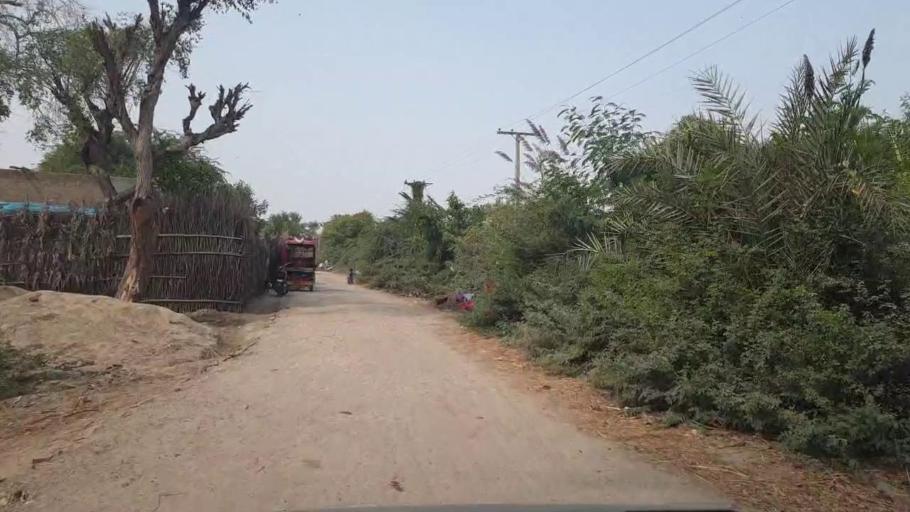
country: PK
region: Sindh
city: Tando Muhammad Khan
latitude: 25.1144
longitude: 68.3680
